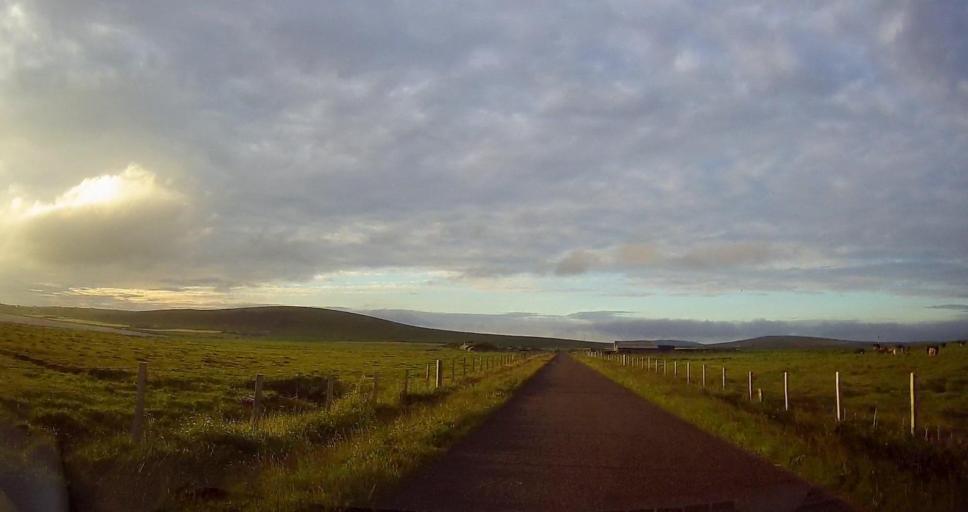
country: GB
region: Scotland
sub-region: Orkney Islands
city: Stromness
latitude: 59.1056
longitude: -3.2562
